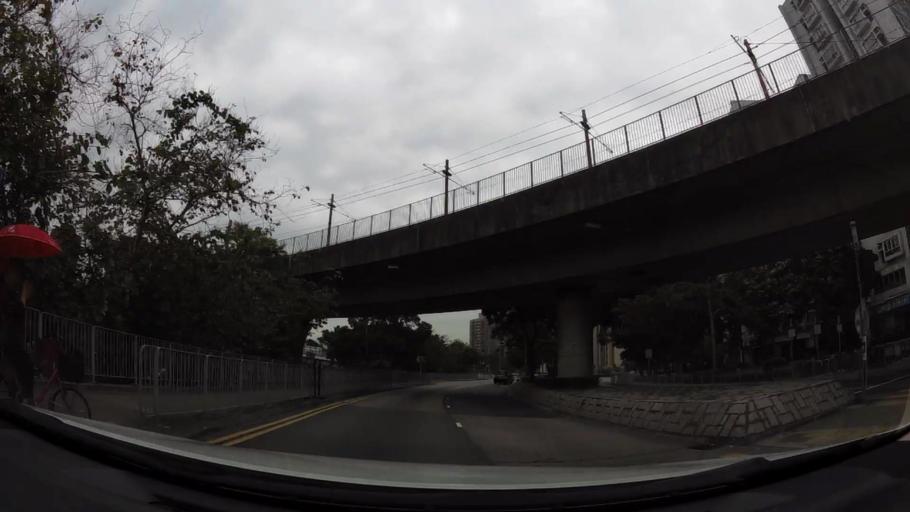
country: HK
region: Tuen Mun
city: Tuen Mun
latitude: 22.4077
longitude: 113.9788
